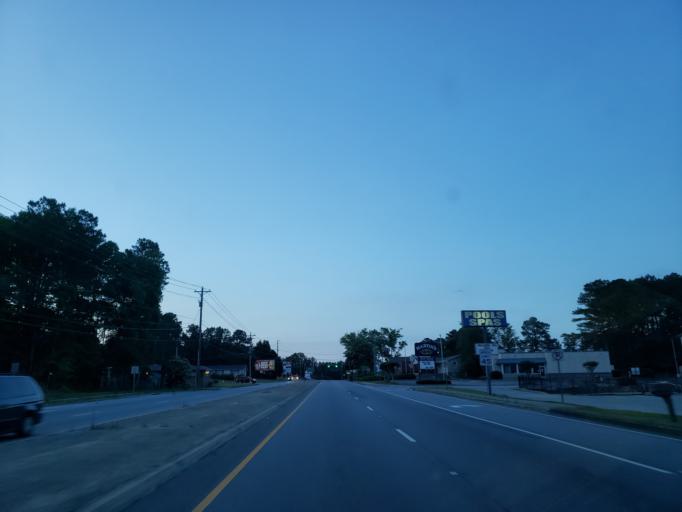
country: US
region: Georgia
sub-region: Douglas County
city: Douglasville
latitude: 33.7108
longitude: -84.7699
